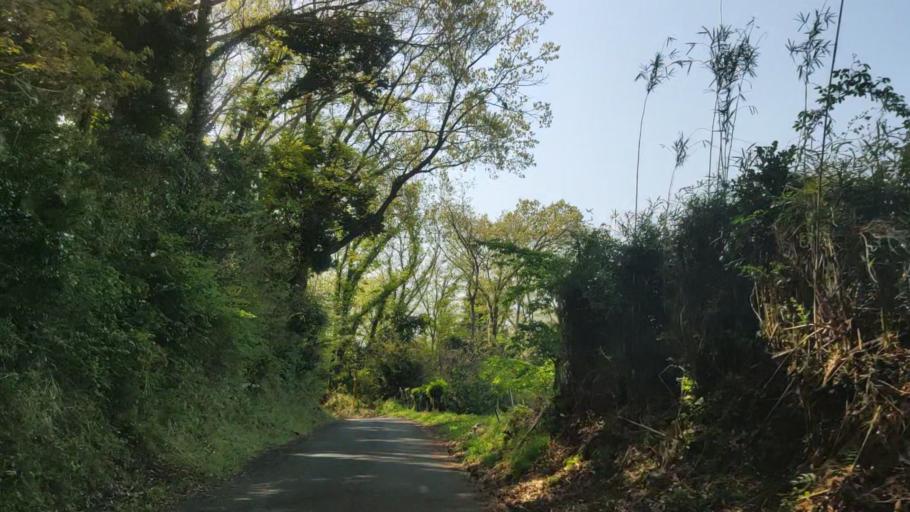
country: JP
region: Kanagawa
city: Ninomiya
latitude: 35.3258
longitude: 139.2675
